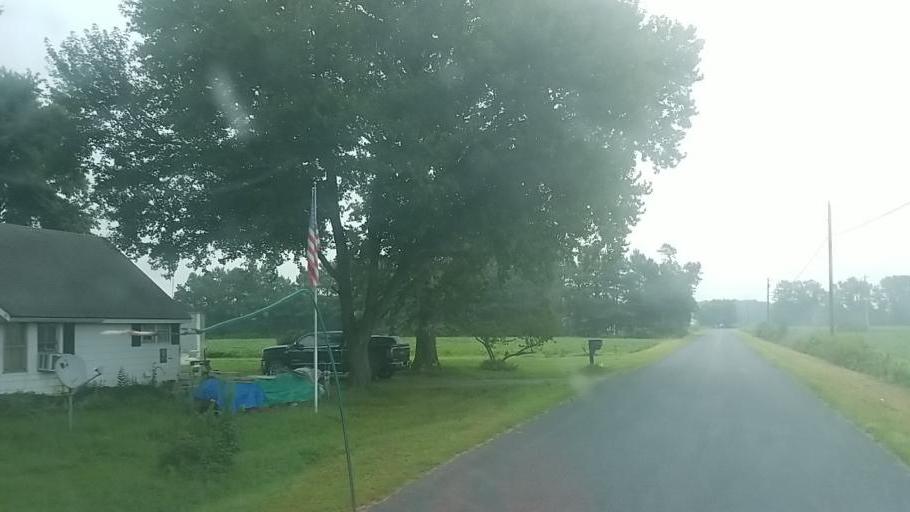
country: US
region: Maryland
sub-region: Wicomico County
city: Pittsville
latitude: 38.4498
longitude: -75.3518
